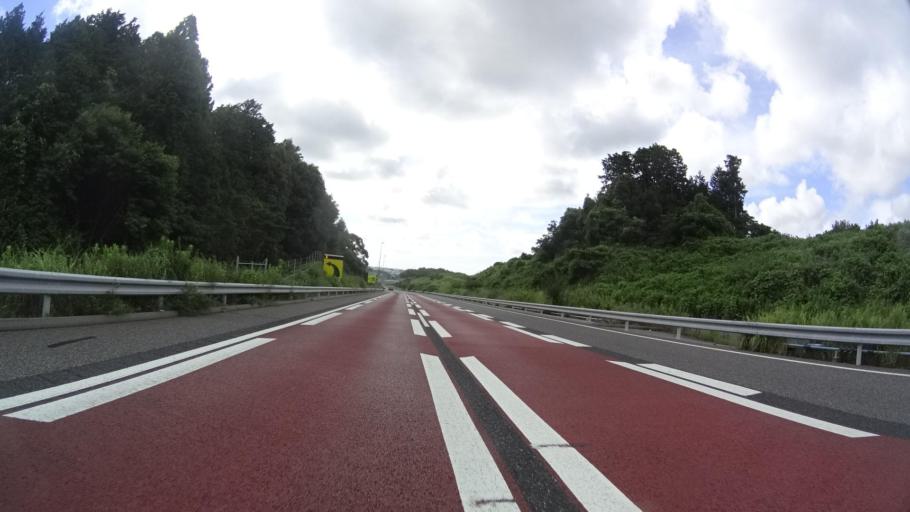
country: JP
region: Mie
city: Kameyama
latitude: 34.8978
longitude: 136.4518
